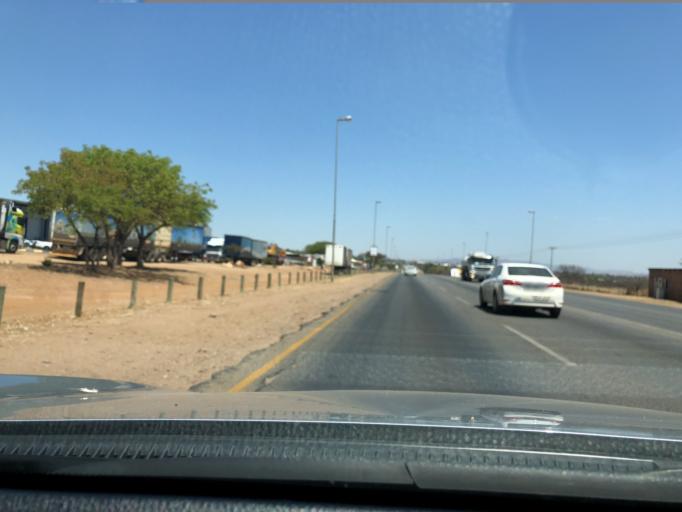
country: ZA
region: Limpopo
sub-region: Capricorn District Municipality
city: Polokwane
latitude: -23.8632
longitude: 29.4697
